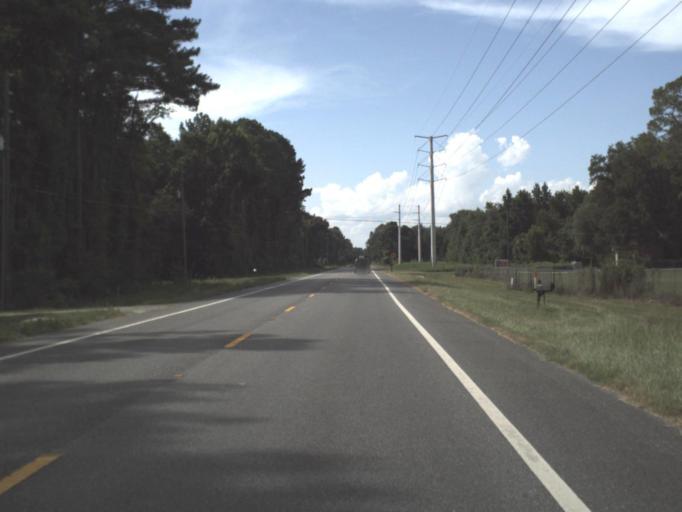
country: US
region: Florida
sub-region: Taylor County
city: Perry
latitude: 30.1551
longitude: -83.5919
